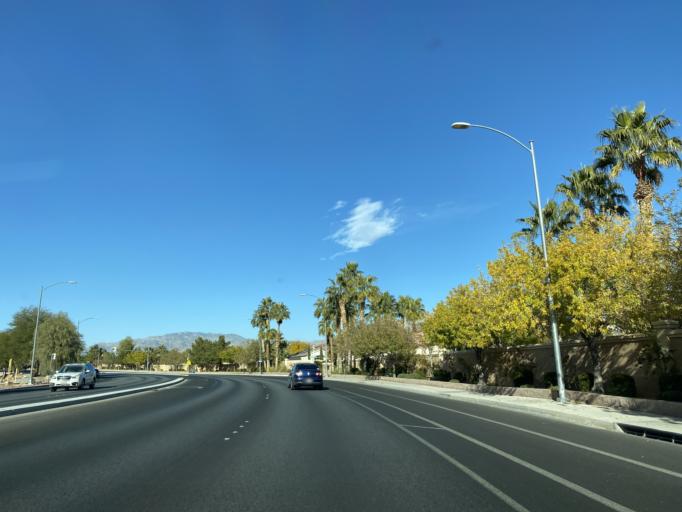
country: US
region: Nevada
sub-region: Clark County
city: Las Vegas
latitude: 36.2935
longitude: -115.2593
